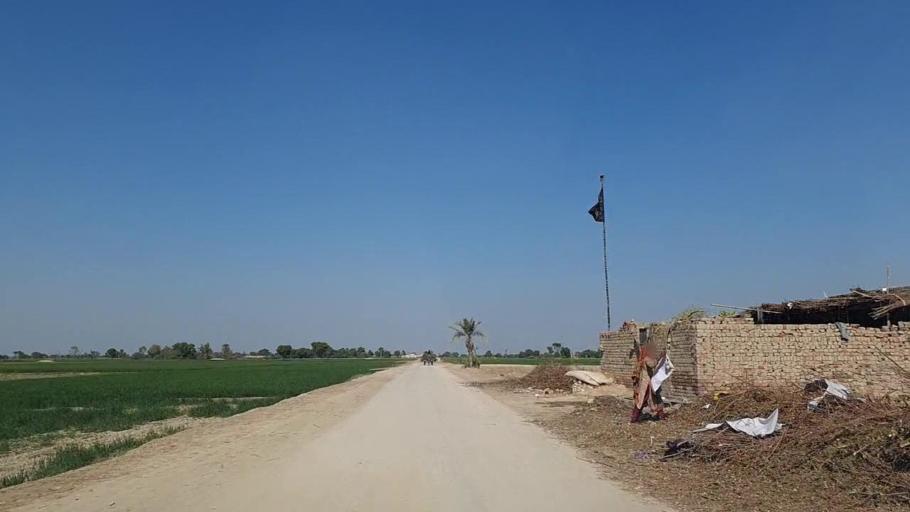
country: PK
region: Sindh
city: Nawabshah
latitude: 26.2511
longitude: 68.4513
